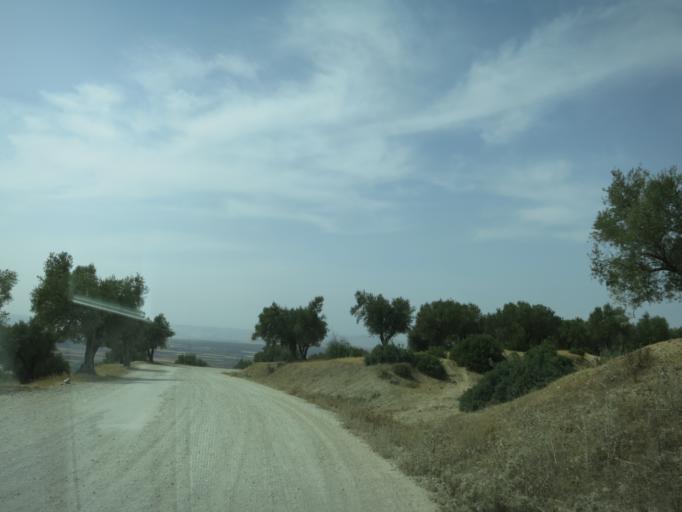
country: MA
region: Meknes-Tafilalet
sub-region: Meknes
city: Meknes
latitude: 34.0621
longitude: -5.5289
